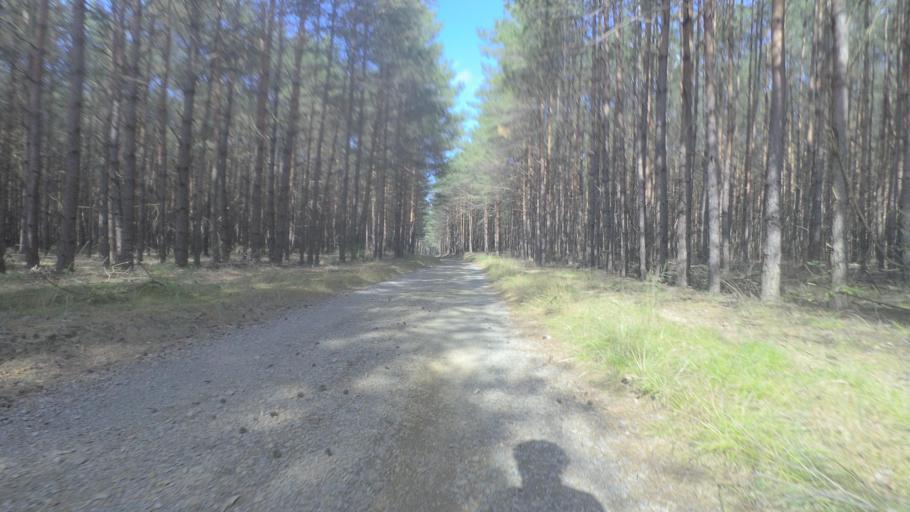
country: DE
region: Brandenburg
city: Munchehofe
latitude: 52.1781
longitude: 13.8721
